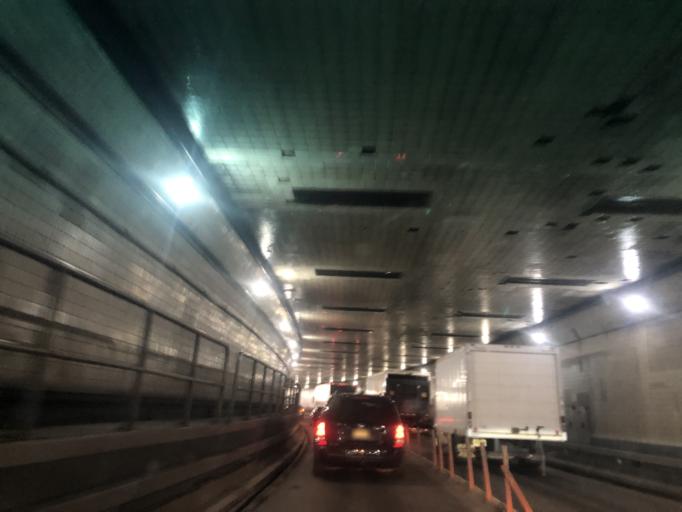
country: US
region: New Jersey
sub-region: Hudson County
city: Hoboken
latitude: 40.7577
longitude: -74.0289
